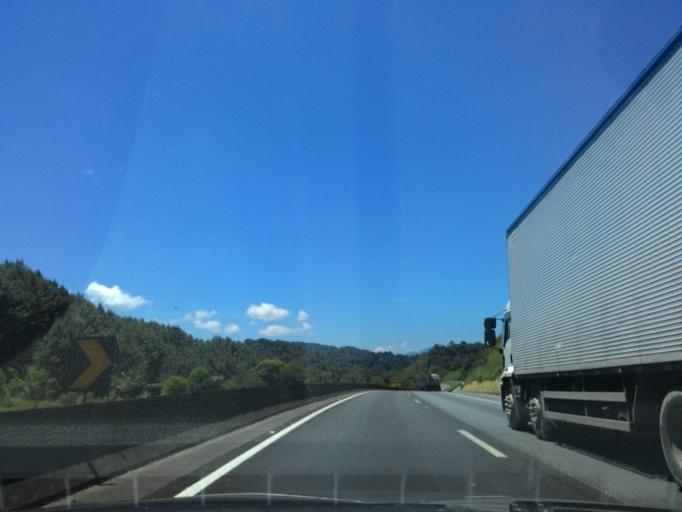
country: BR
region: Parana
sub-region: Antonina
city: Antonina
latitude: -25.1001
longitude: -48.6954
